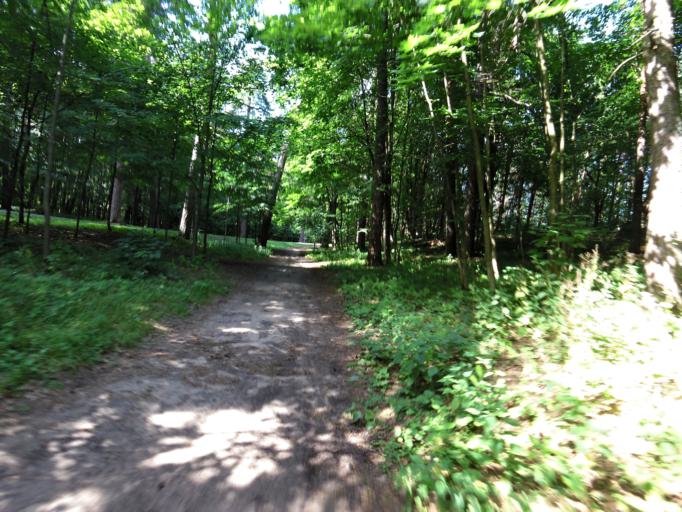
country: LT
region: Vilnius County
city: Vilkpede
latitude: 54.6871
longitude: 25.2439
